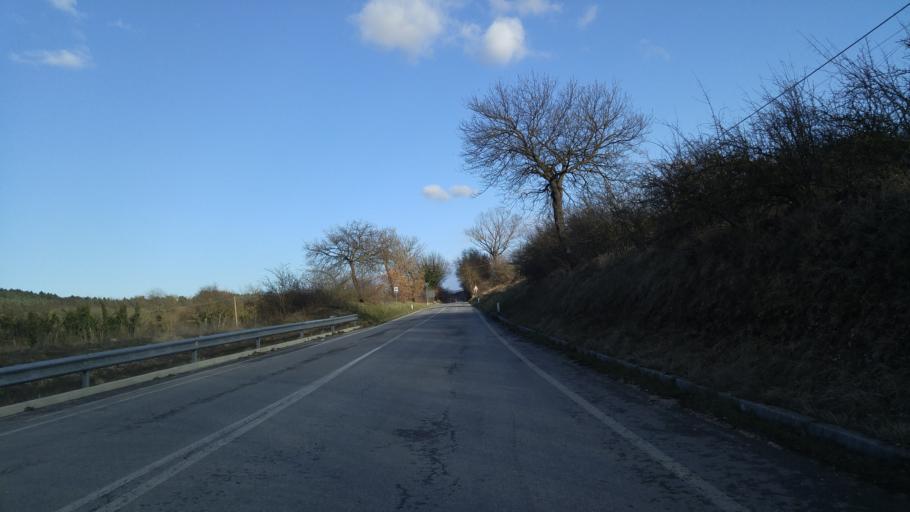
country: IT
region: The Marches
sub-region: Provincia di Pesaro e Urbino
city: Cagli
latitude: 43.5406
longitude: 12.6764
